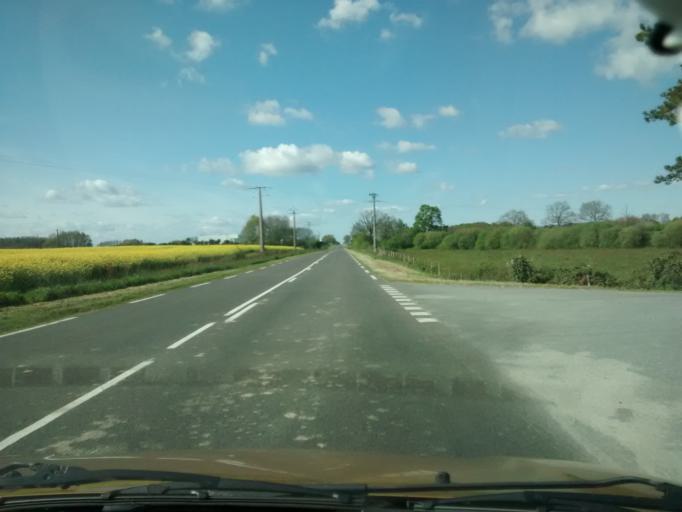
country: FR
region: Pays de la Loire
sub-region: Departement de la Vendee
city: Les Lucs-sur-Boulogne
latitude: 46.8737
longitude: -1.4996
